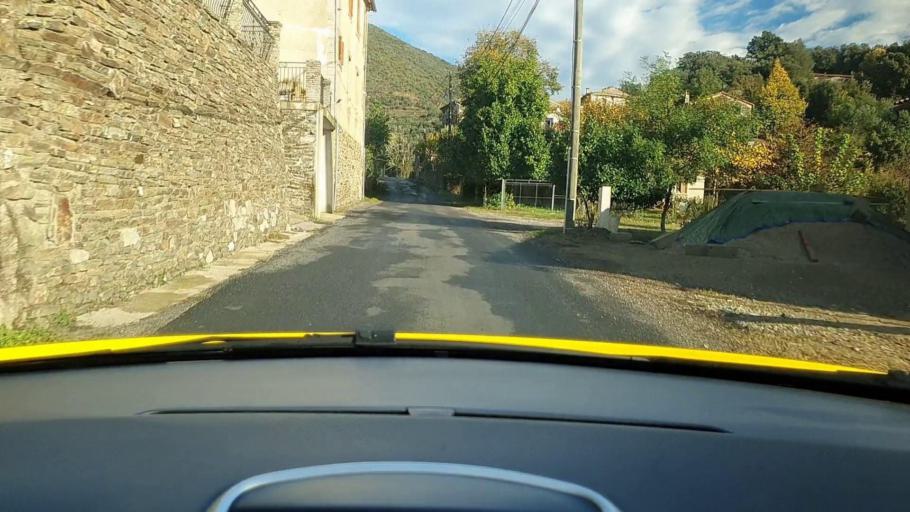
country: FR
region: Languedoc-Roussillon
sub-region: Departement du Gard
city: Sumene
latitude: 44.0073
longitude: 3.7121
